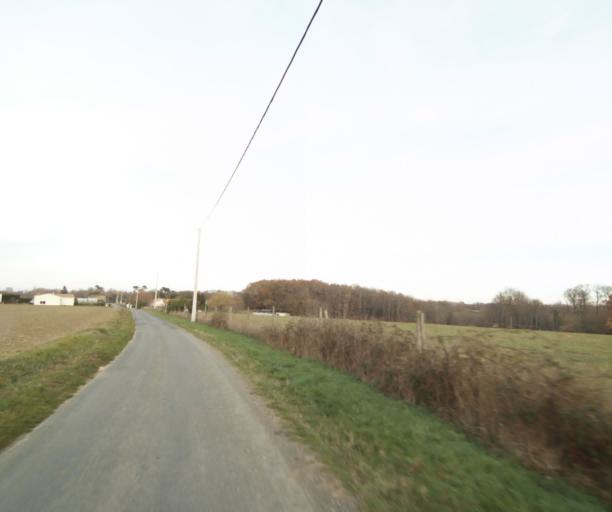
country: FR
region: Poitou-Charentes
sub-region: Departement de la Charente-Maritime
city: Fontcouverte
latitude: 45.7797
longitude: -0.5869
